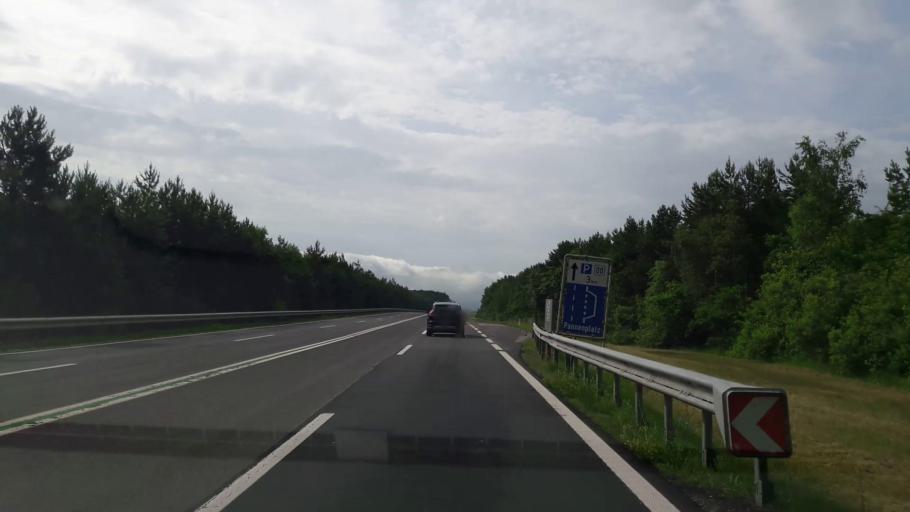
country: AT
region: Burgenland
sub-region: Politischer Bezirk Mattersburg
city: Sieggraben
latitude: 47.6433
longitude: 16.3749
